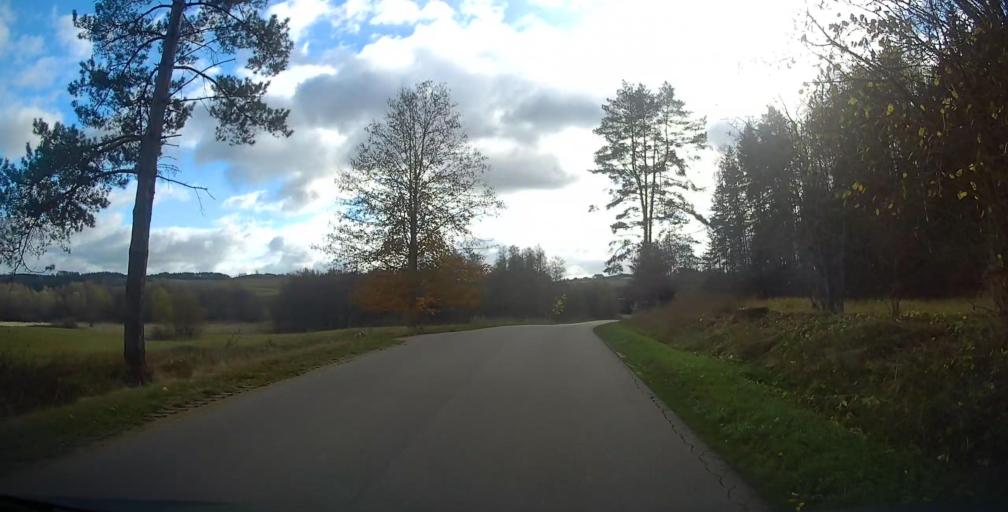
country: PL
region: Podlasie
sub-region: Suwalki
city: Suwalki
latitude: 54.2737
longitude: 22.9087
